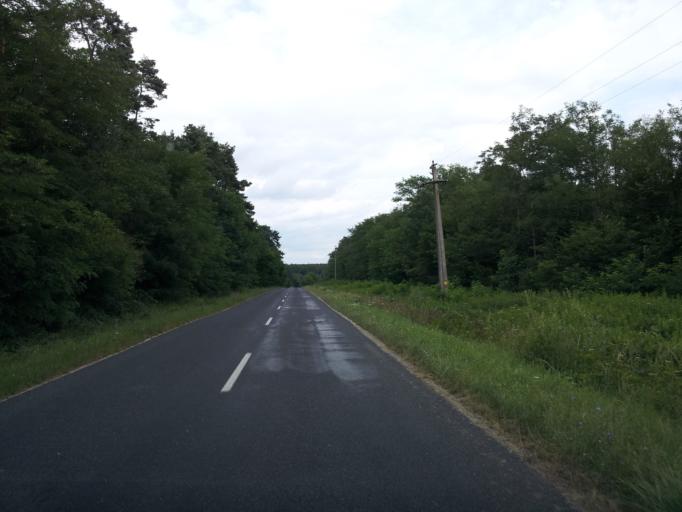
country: HU
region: Zala
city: Turje
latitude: 47.0496
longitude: 17.0040
